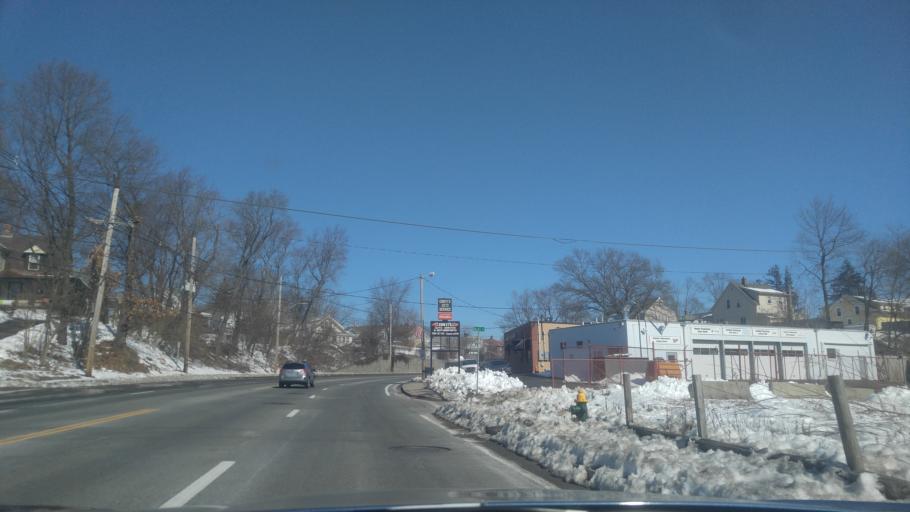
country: US
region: Rhode Island
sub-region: Providence County
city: Cranston
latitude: 41.7706
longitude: -71.4053
